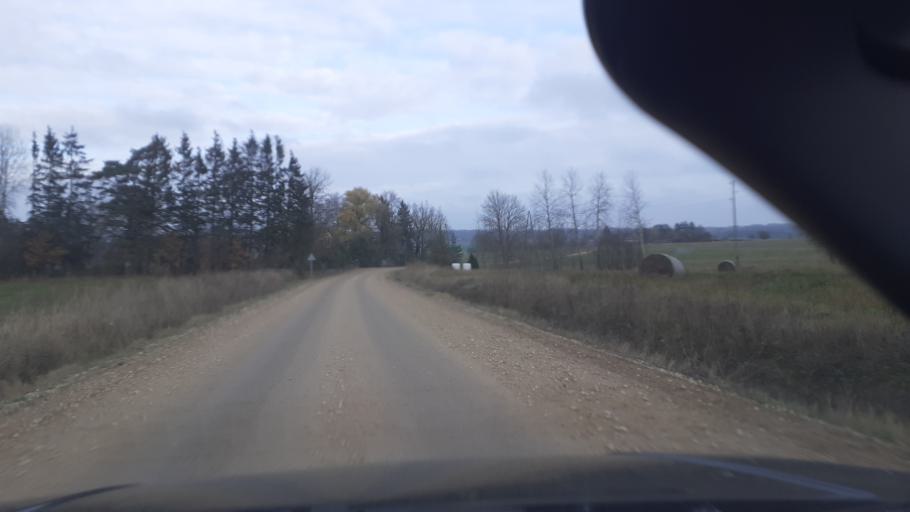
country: LV
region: Aizpute
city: Aizpute
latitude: 56.8634
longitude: 21.6726
